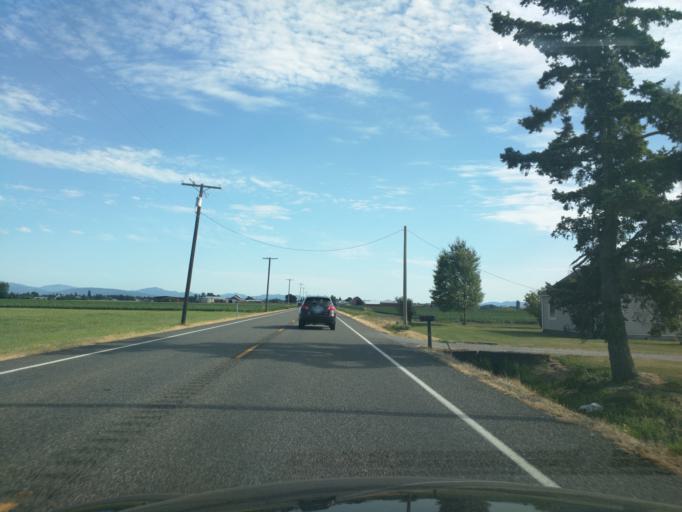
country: US
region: Washington
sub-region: Whatcom County
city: Lynden
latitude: 48.9762
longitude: -122.4852
